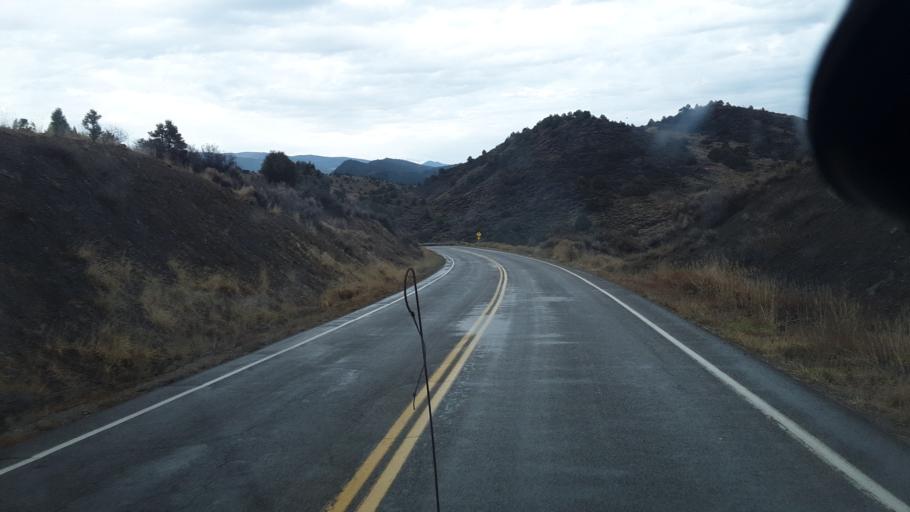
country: US
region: Colorado
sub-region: La Plata County
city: Durango
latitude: 37.2452
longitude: -107.8931
